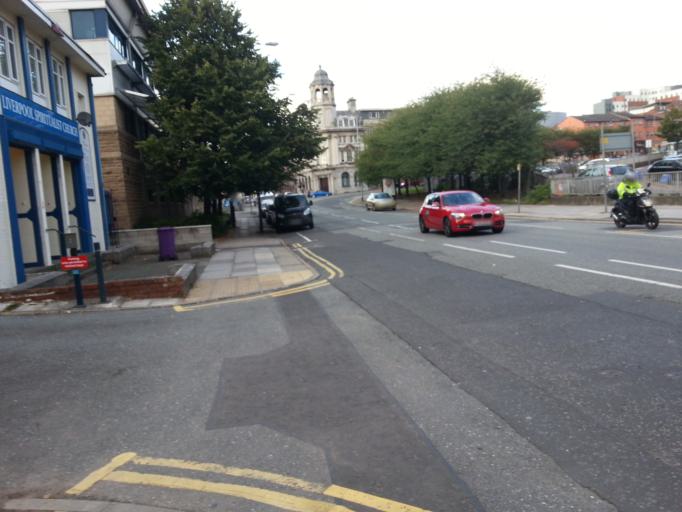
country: GB
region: England
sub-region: Liverpool
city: Liverpool
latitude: 53.4095
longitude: -2.9679
